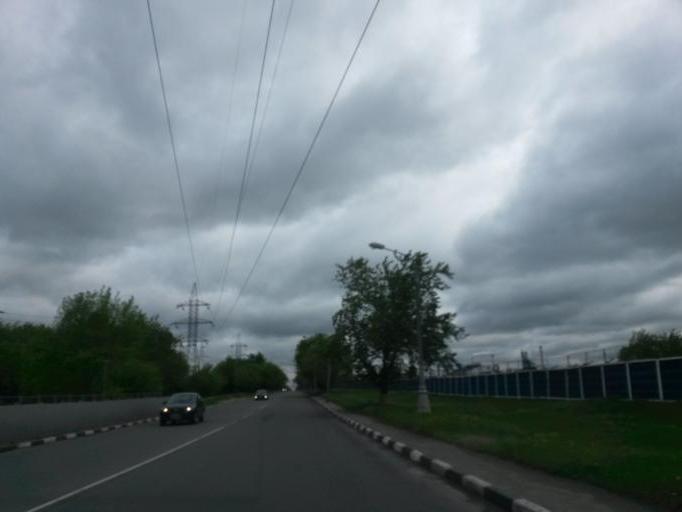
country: RU
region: Moscow
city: Kapotnya
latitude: 55.6447
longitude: 37.7888
